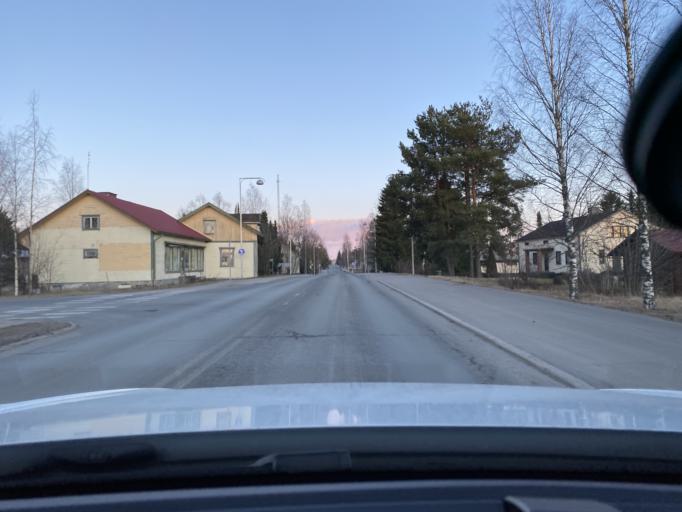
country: FI
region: Pirkanmaa
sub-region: Lounais-Pirkanmaa
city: Punkalaidun
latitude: 61.1172
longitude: 23.0866
